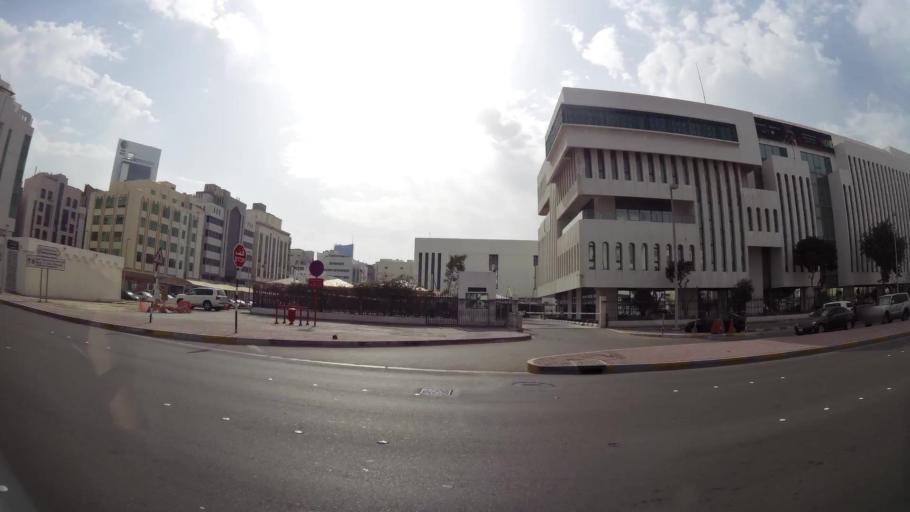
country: AE
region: Abu Dhabi
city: Abu Dhabi
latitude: 24.4605
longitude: 54.3858
